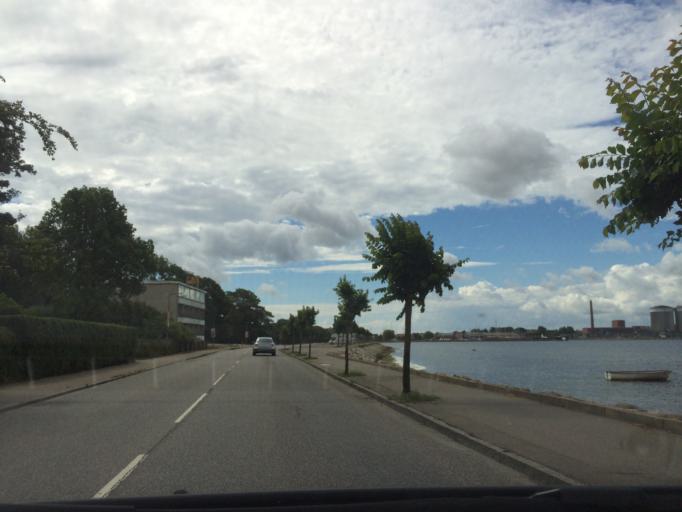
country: DK
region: Zealand
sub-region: Vordingborg Kommune
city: Stege
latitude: 54.9898
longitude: 12.2796
